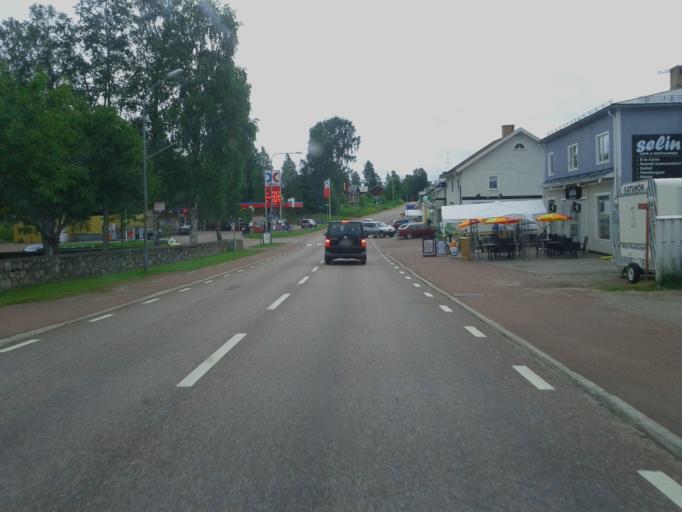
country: NO
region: Hedmark
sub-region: Trysil
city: Innbygda
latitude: 61.6933
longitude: 13.1396
